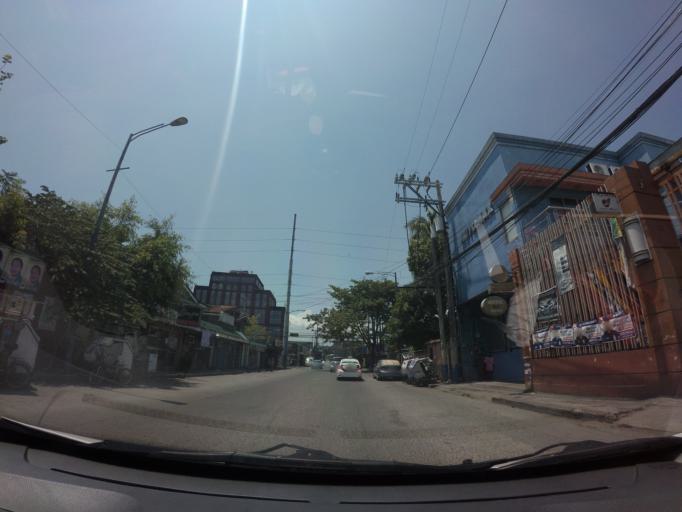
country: PH
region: Metro Manila
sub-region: Makati City
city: Makati City
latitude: 14.5566
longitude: 121.0019
